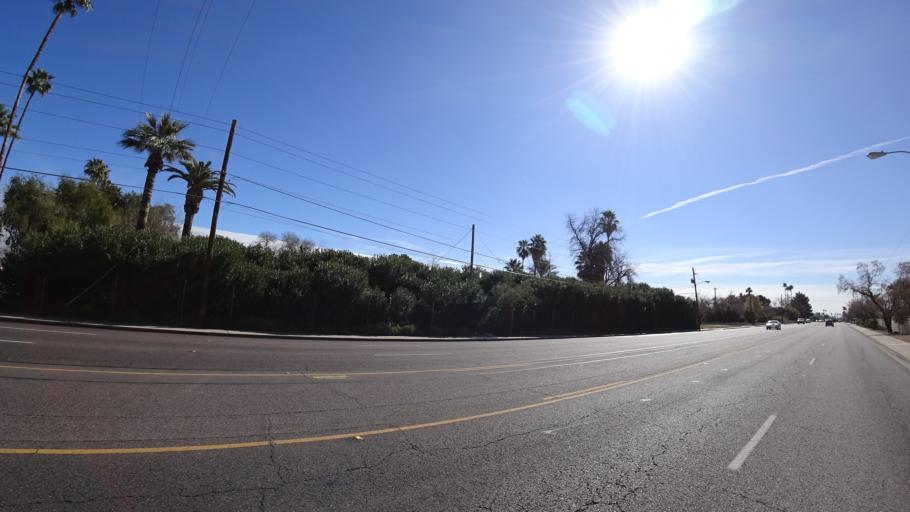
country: US
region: Arizona
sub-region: Maricopa County
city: Glendale
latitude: 33.5565
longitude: -112.1863
